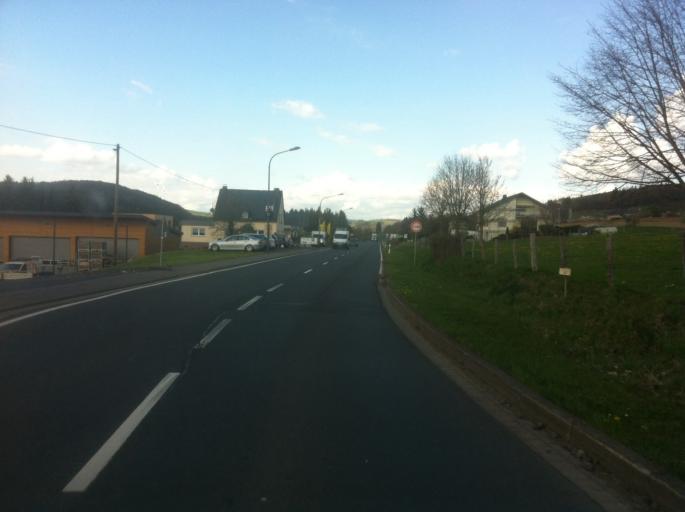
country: DE
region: Rheinland-Pfalz
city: Pronsfeld
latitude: 50.1614
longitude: 6.3423
